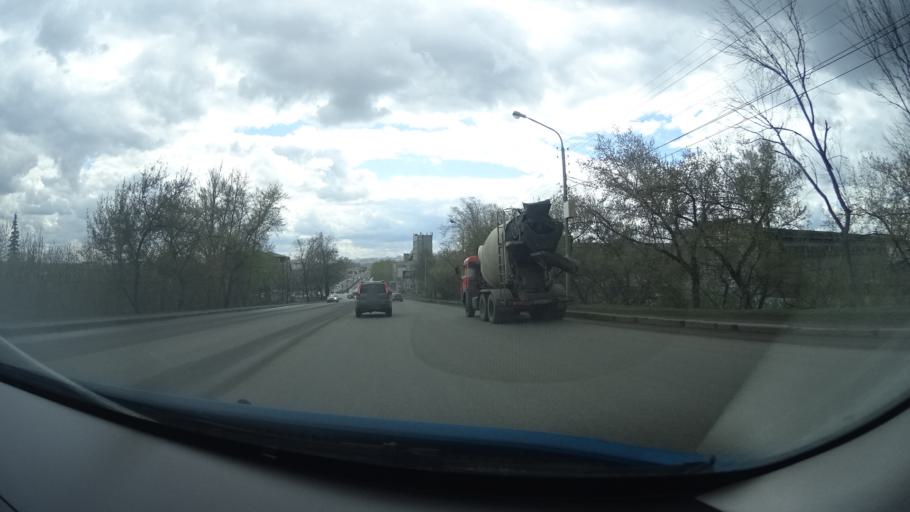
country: RU
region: Bashkortostan
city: Ufa
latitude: 54.8084
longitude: 56.0853
